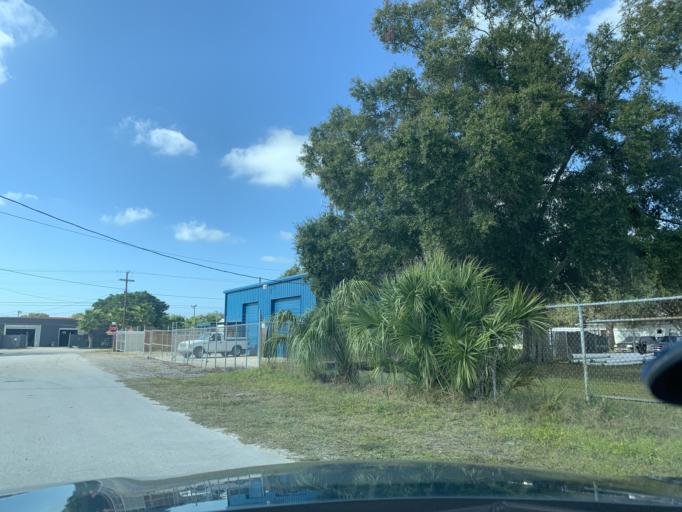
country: US
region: Florida
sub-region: Pinellas County
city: Belleair
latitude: 27.9380
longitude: -82.7950
